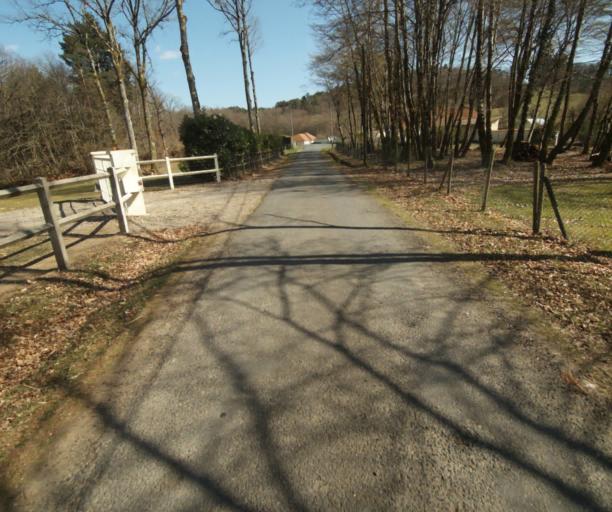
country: FR
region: Limousin
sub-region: Departement de la Correze
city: Saint-Mexant
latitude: 45.2856
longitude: 1.6423
